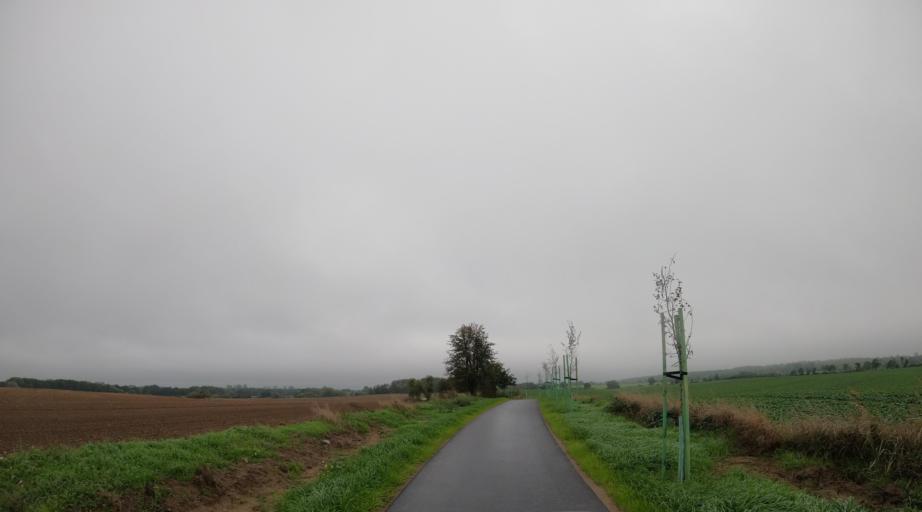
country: PL
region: West Pomeranian Voivodeship
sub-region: Powiat mysliborski
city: Mysliborz
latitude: 52.9244
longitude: 14.7348
